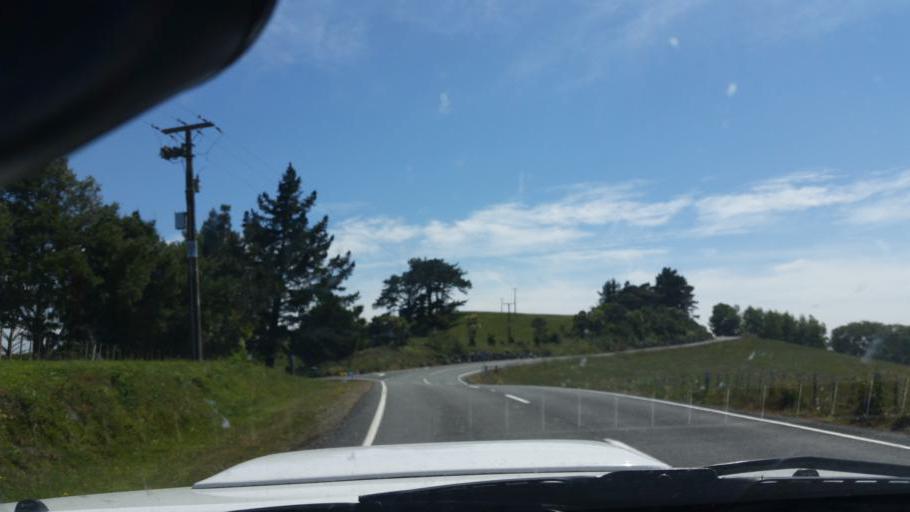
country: NZ
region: Auckland
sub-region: Auckland
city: Wellsford
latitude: -36.2247
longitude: 174.3746
